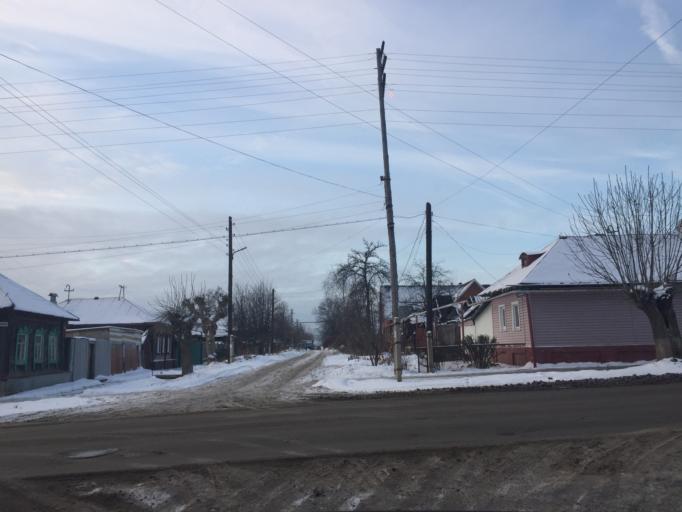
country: RU
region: Tula
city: Tula
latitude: 54.2035
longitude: 37.6592
